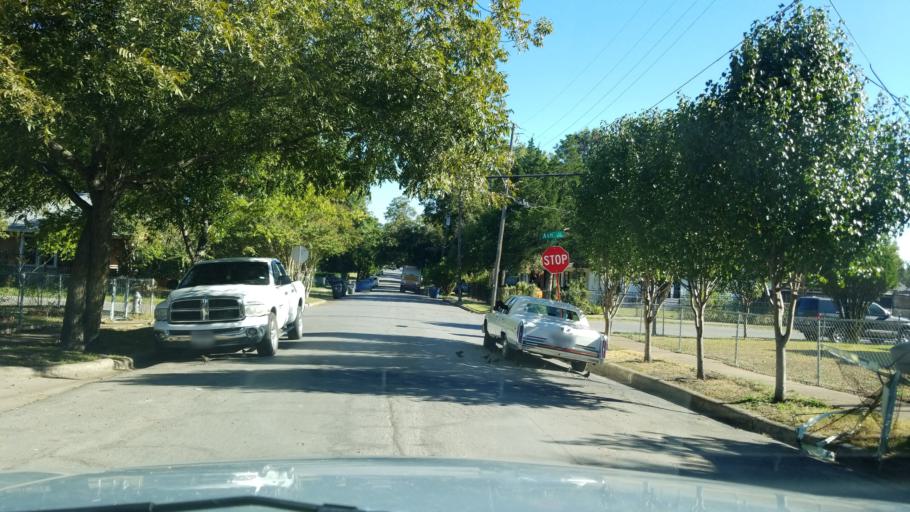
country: US
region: Texas
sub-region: Dallas County
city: Highland Park
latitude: 32.7989
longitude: -96.7518
